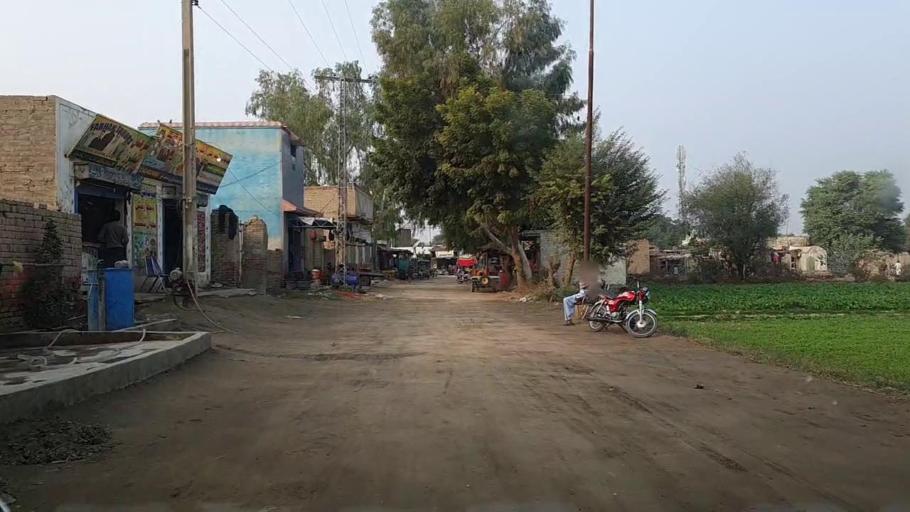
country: PK
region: Sindh
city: Setharja Old
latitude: 27.0856
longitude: 68.4951
